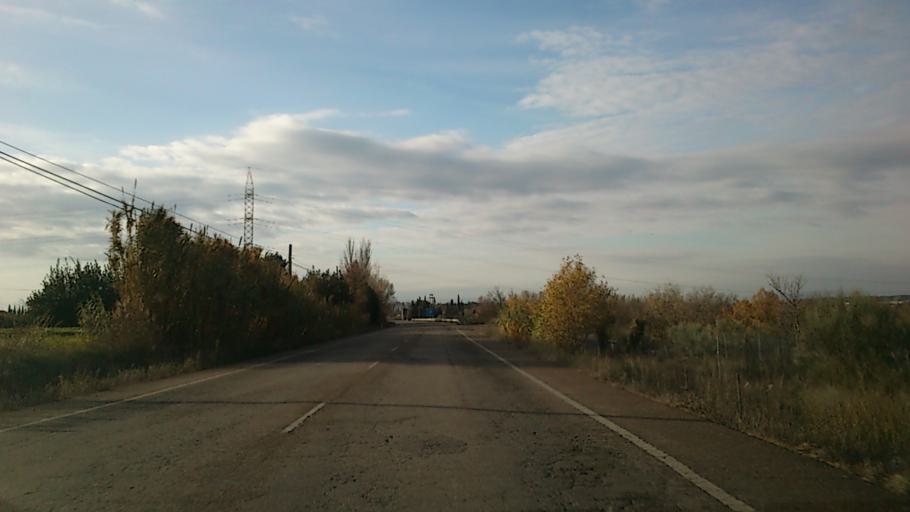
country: ES
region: Aragon
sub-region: Provincia de Zaragoza
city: Villanueva de Gallego
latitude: 41.7449
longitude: -0.8048
